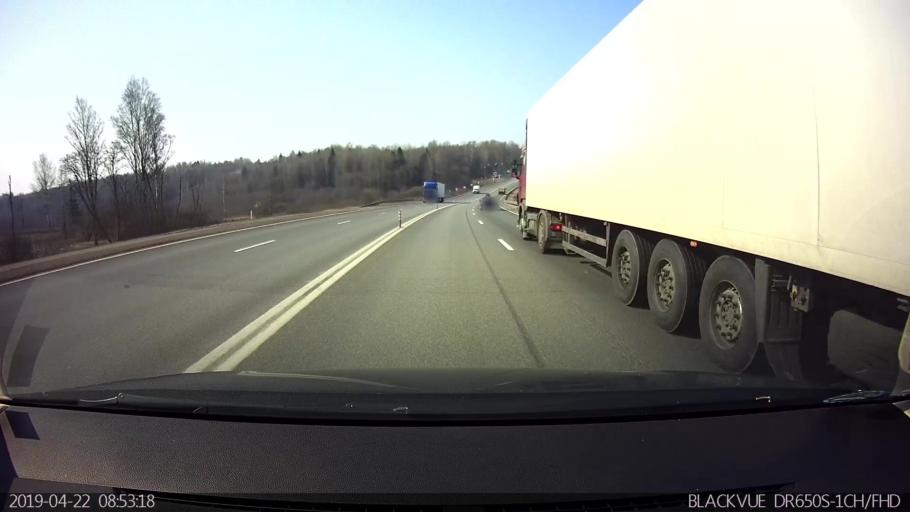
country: RU
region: Smolensk
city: Pechersk
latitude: 54.8956
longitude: 32.1159
